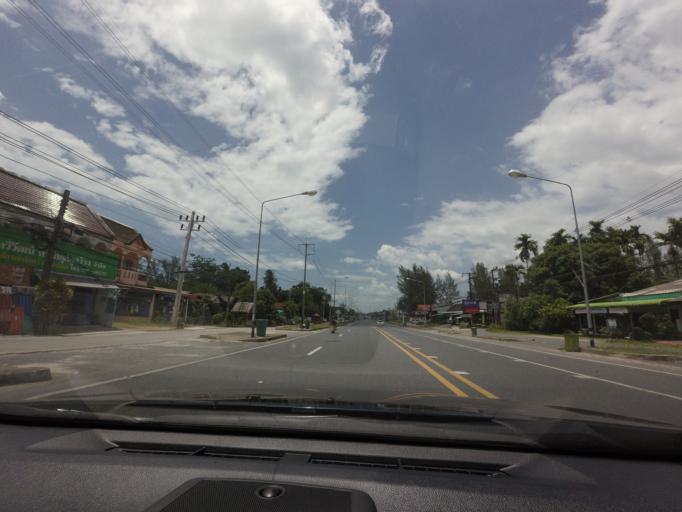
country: TH
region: Phangnga
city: Ban Khao Lak
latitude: 8.6599
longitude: 98.2533
